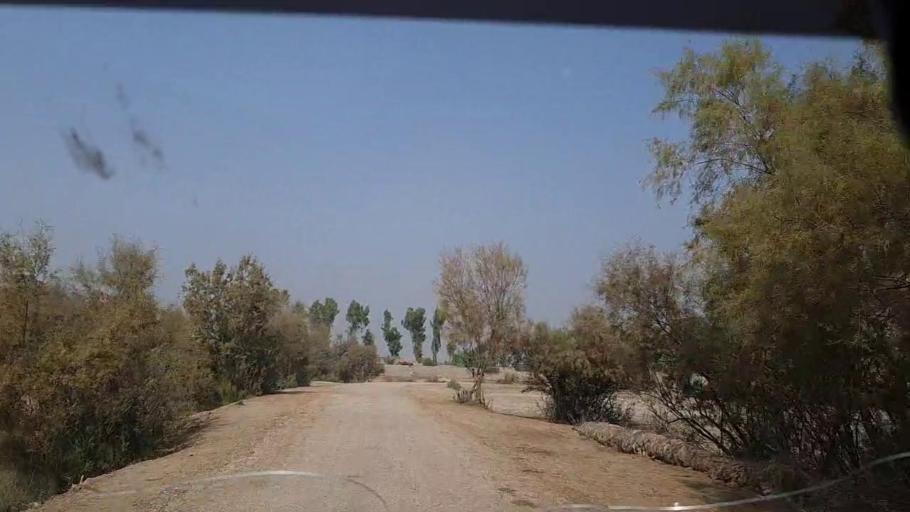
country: PK
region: Sindh
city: Shikarpur
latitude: 28.0912
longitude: 68.6686
